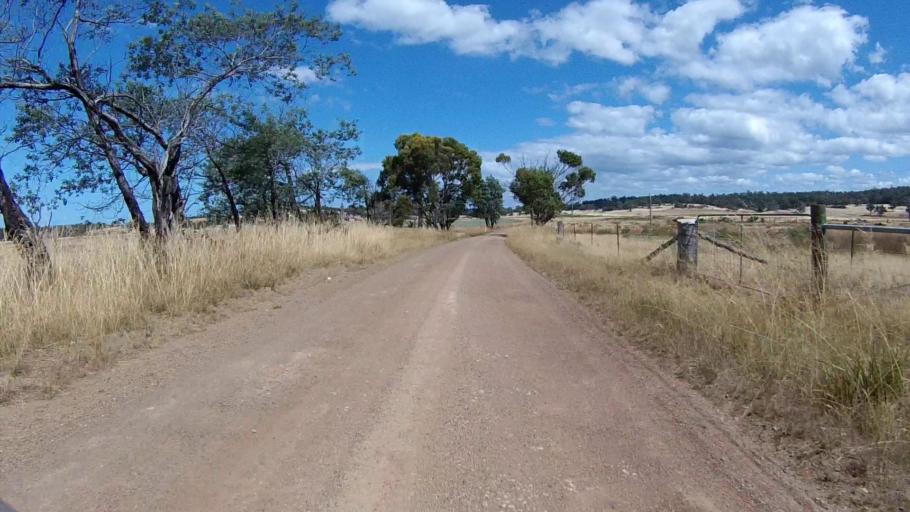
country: AU
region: Tasmania
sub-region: Break O'Day
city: St Helens
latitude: -41.9548
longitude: 148.0699
